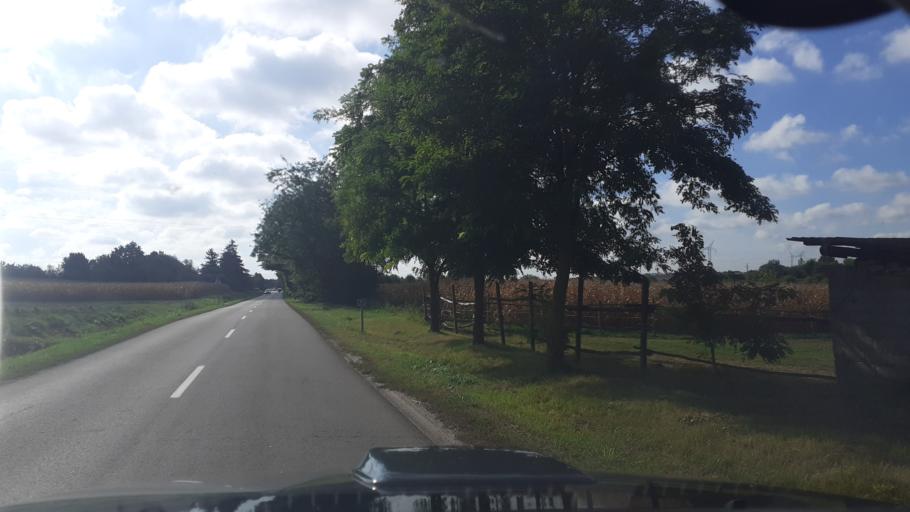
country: HU
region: Fejer
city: Baracs
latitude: 46.9055
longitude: 18.8928
